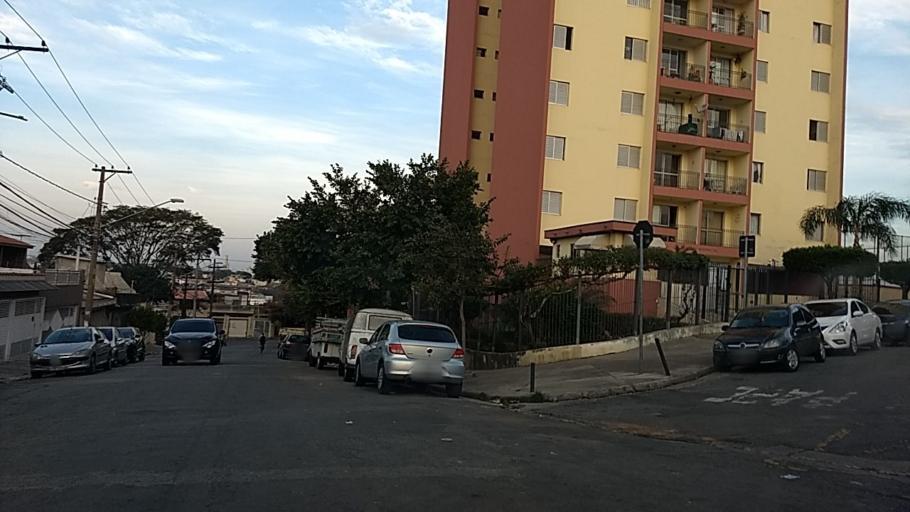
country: BR
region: Sao Paulo
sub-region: Guarulhos
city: Guarulhos
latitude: -23.5029
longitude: -46.5780
